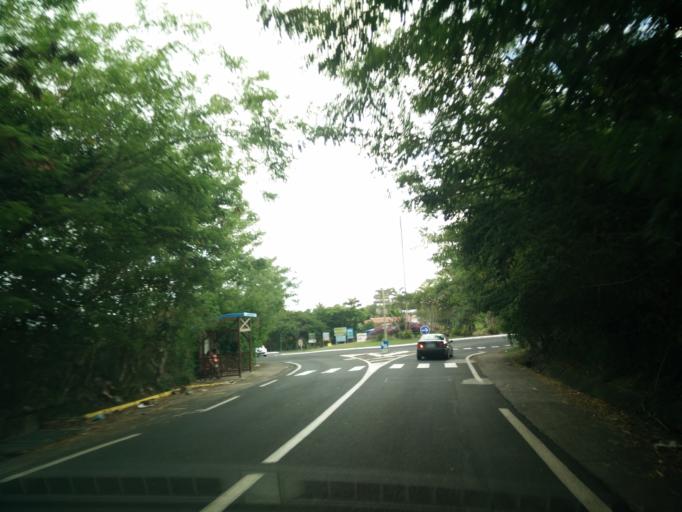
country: MQ
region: Martinique
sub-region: Martinique
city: Le Marin
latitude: 14.4627
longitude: -60.8587
